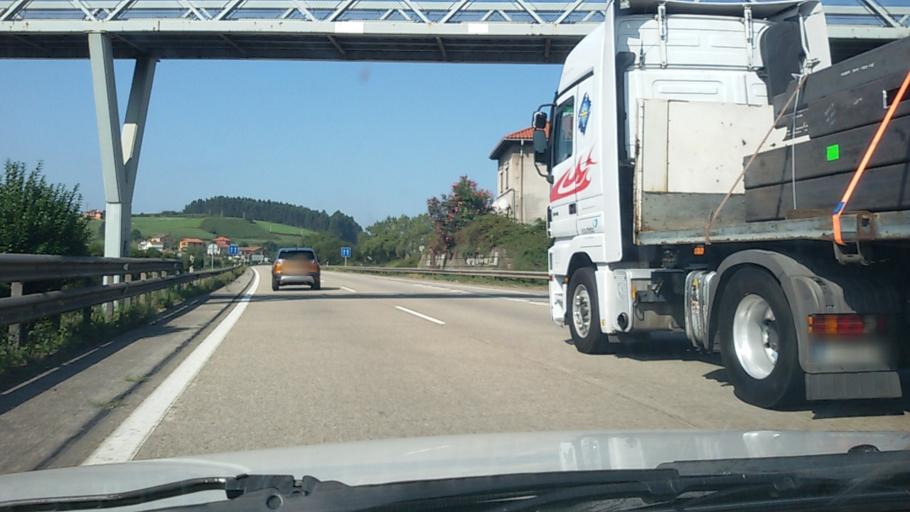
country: ES
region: Asturias
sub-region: Province of Asturias
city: Corvera de Asturias
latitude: 43.5503
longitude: -5.8738
